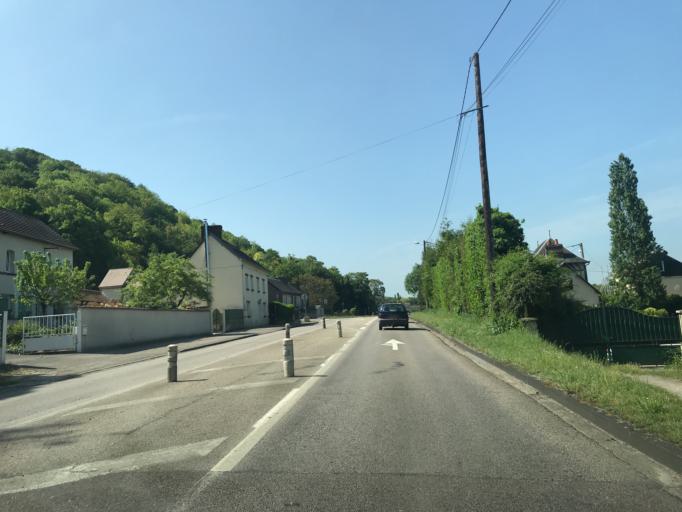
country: FR
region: Haute-Normandie
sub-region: Departement de la Seine-Maritime
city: Les Authieux-sur-le-Port-Saint-Ouen
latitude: 49.3405
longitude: 1.1214
